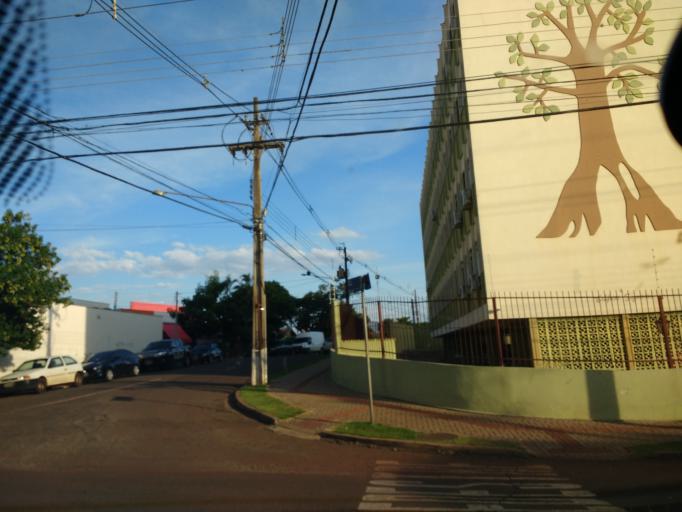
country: BR
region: Parana
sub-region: Londrina
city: Londrina
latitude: -23.2955
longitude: -51.1437
